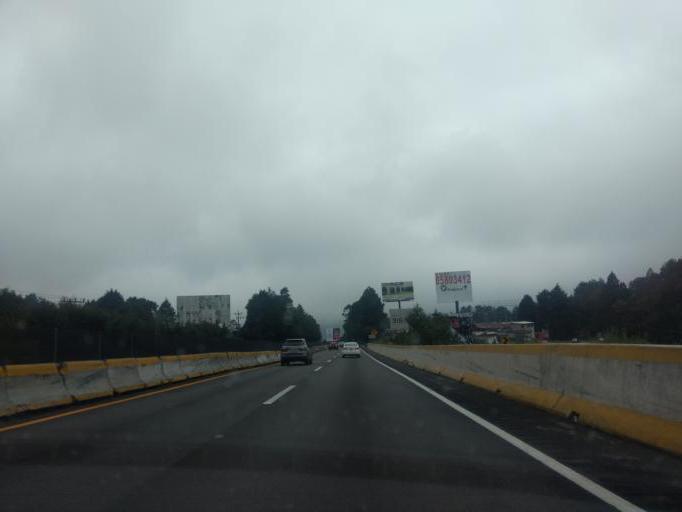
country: MX
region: Morelos
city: Tres Marias
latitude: 19.0721
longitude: -99.2360
